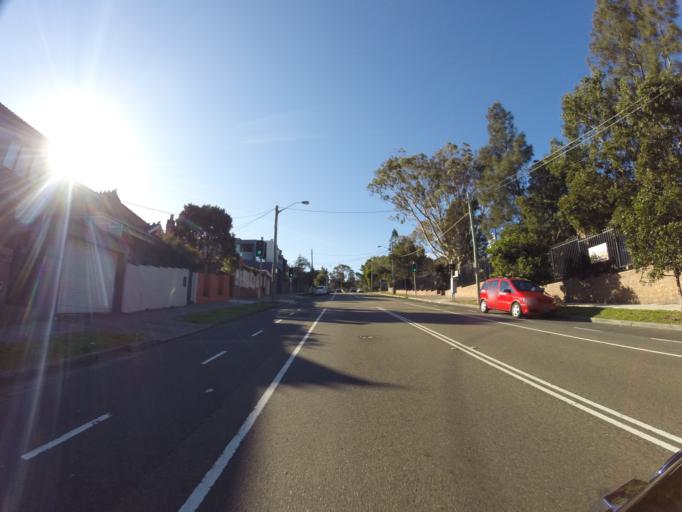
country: AU
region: New South Wales
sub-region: Randwick
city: Clovelly
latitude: -33.9078
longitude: 151.2596
